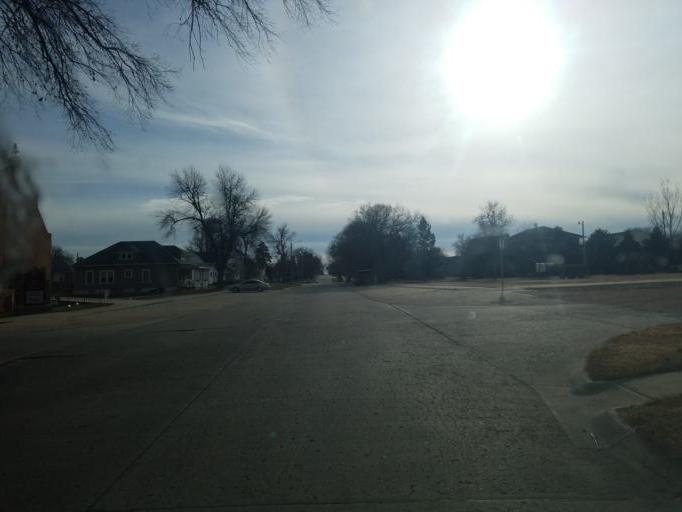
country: US
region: Nebraska
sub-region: Knox County
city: Creighton
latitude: 42.4635
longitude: -97.9063
